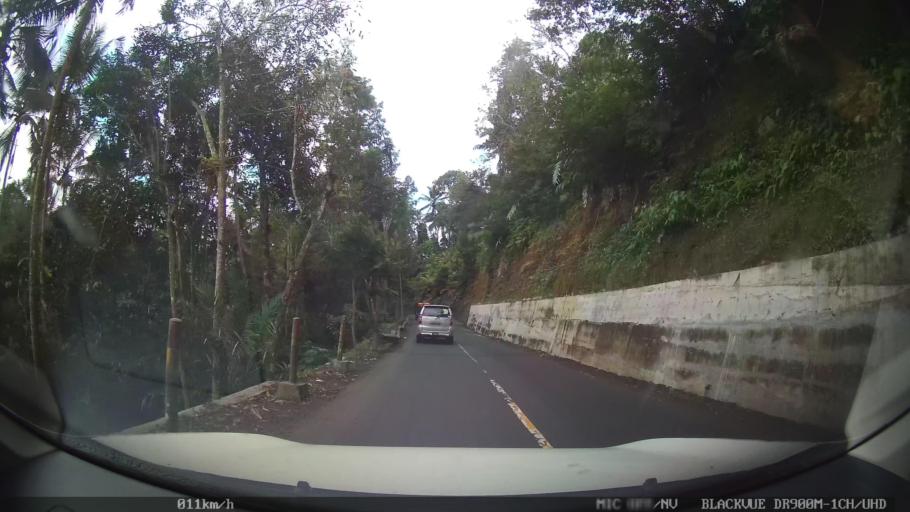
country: ID
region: Bali
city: Banjar Kubu
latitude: -8.4078
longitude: 115.4238
